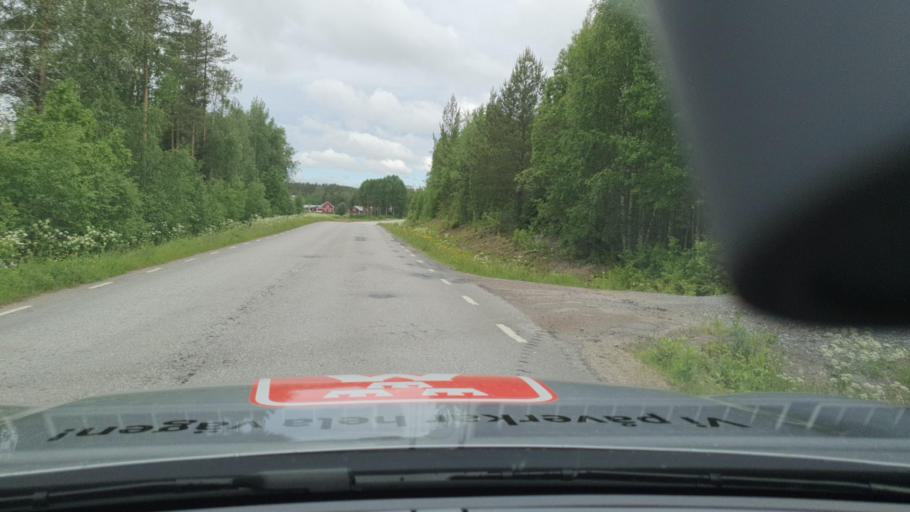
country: SE
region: Norrbotten
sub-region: Lulea Kommun
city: Ranea
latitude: 65.9486
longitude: 22.1395
